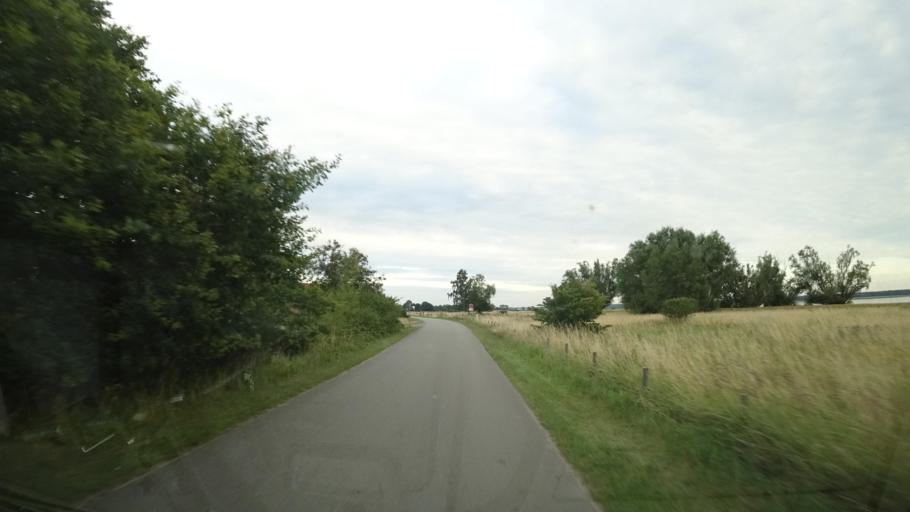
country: DE
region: Mecklenburg-Vorpommern
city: Kemnitz
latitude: 54.1117
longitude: 13.4838
